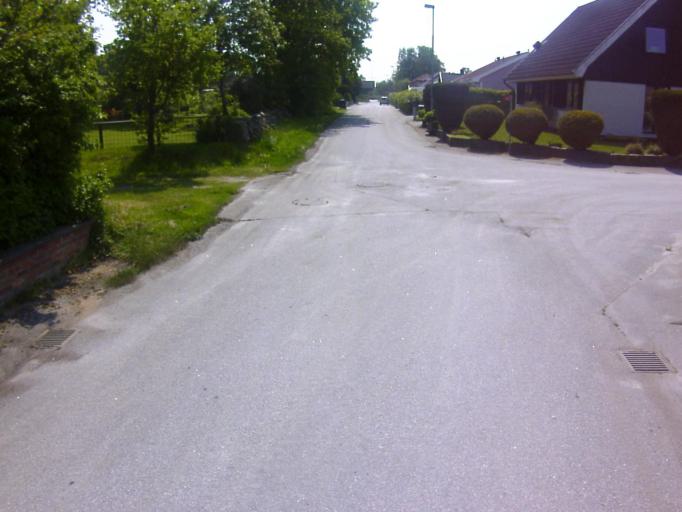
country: SE
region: Blekinge
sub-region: Karlshamns Kommun
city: Morrum
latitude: 56.1274
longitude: 14.6718
